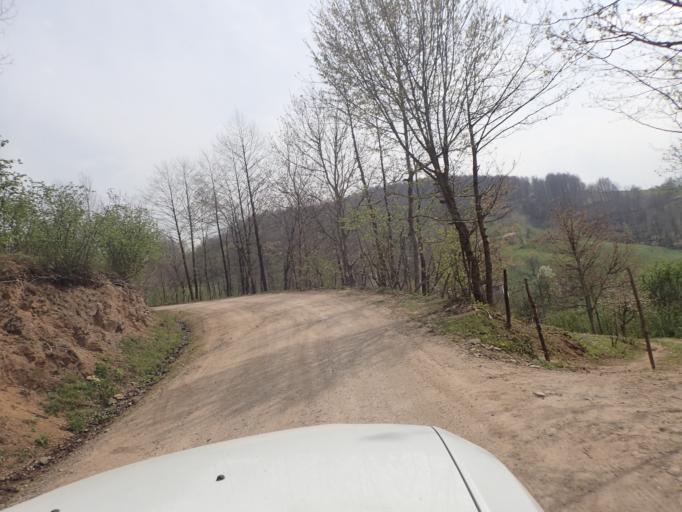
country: TR
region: Ordu
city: Aybasti
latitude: 40.7037
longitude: 37.2894
